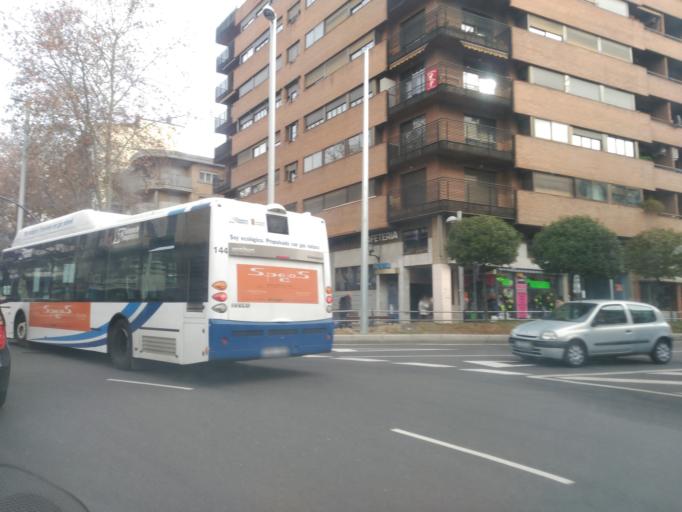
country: ES
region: Castille and Leon
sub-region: Provincia de Salamanca
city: Salamanca
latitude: 40.9724
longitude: -5.6631
